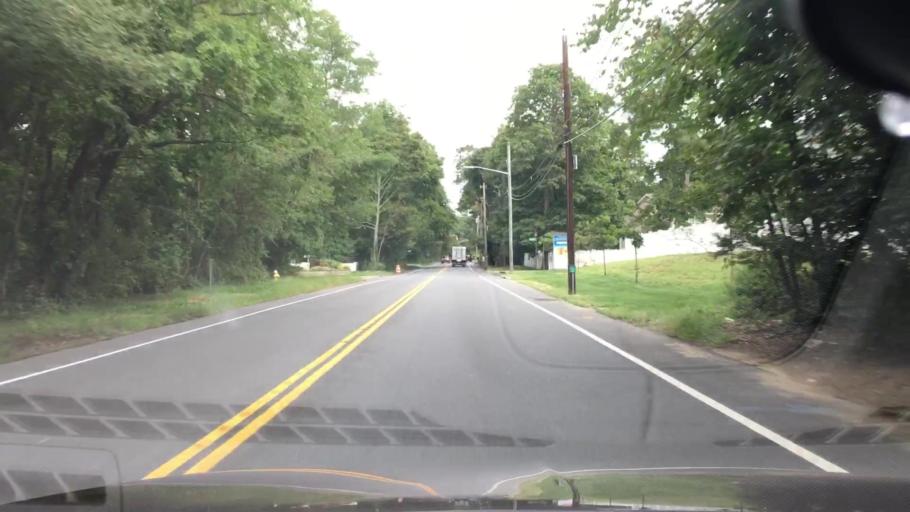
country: US
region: New York
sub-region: Suffolk County
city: Village of the Branch
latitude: 40.8424
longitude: -73.1910
